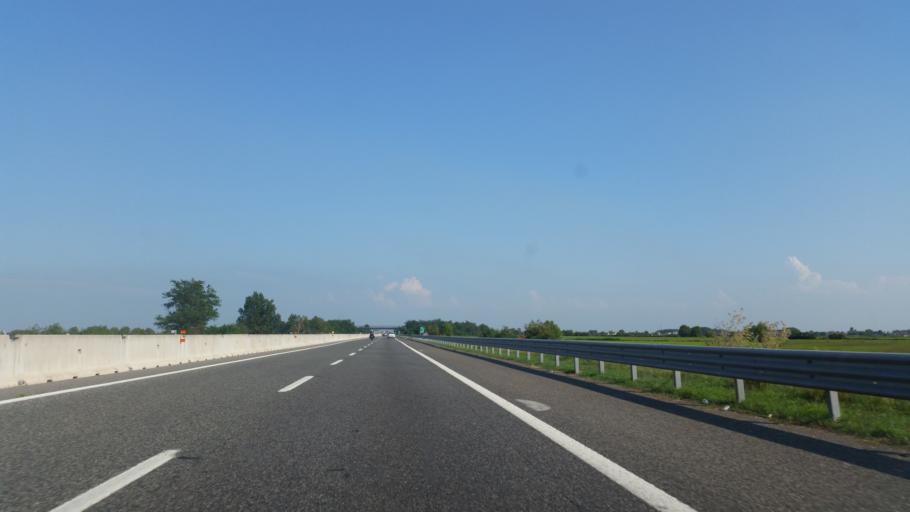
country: IT
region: Piedmont
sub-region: Provincia di Vercelli
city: Asigliano Vercellese
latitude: 45.2823
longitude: 8.4023
